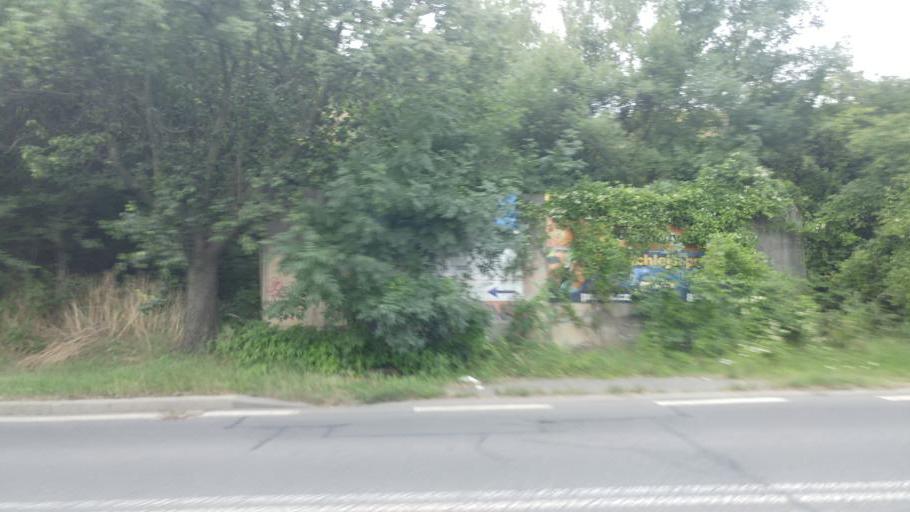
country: CZ
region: Central Bohemia
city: Roztoky
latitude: 50.1282
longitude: 14.3896
